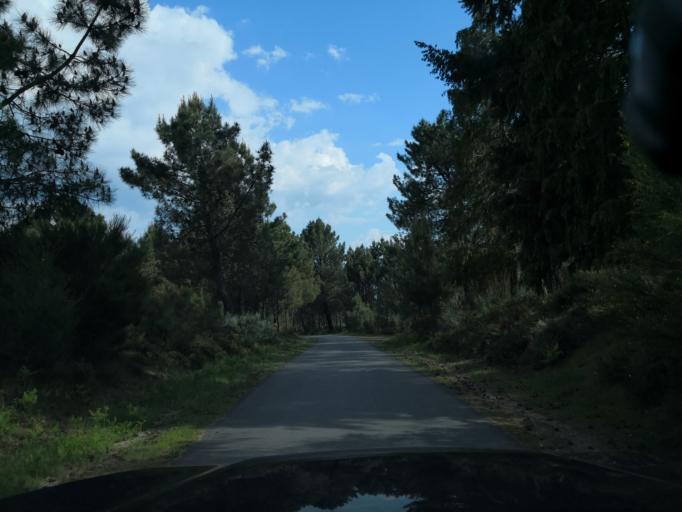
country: PT
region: Vila Real
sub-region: Vila Real
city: Vila Real
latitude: 41.3596
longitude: -7.7381
